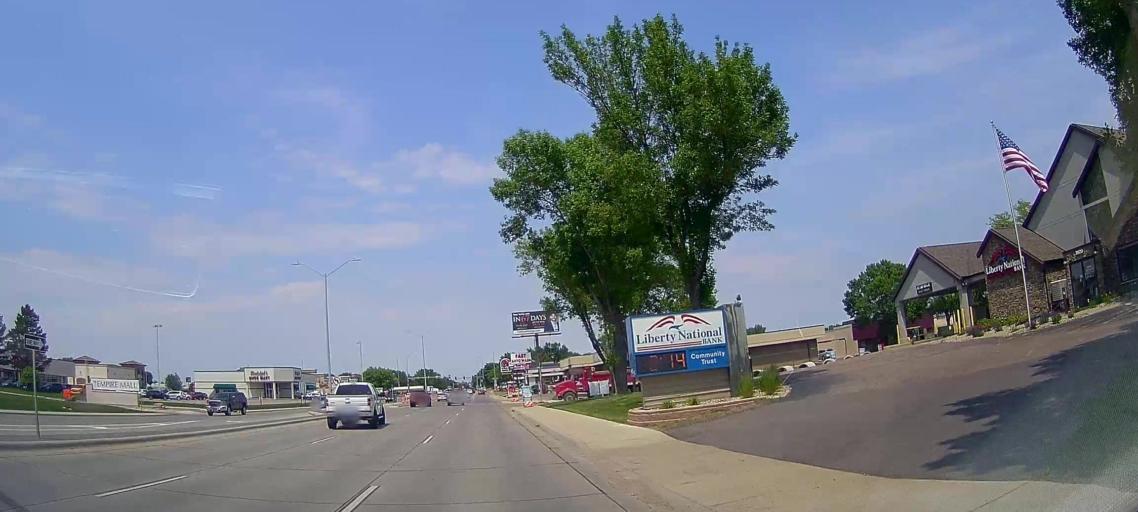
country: US
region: South Dakota
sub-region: Minnehaha County
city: Sioux Falls
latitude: 43.5126
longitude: -96.7710
